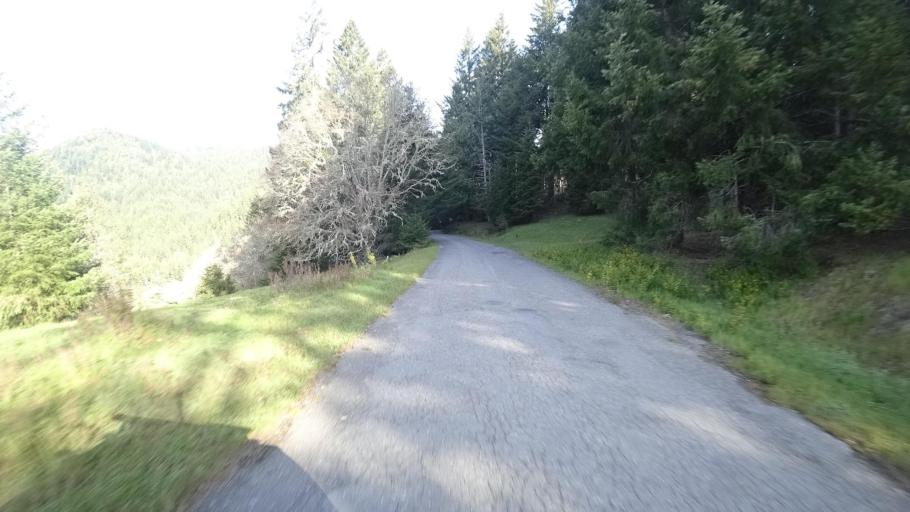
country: US
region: California
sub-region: Humboldt County
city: Bayside
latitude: 40.6919
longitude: -123.9411
